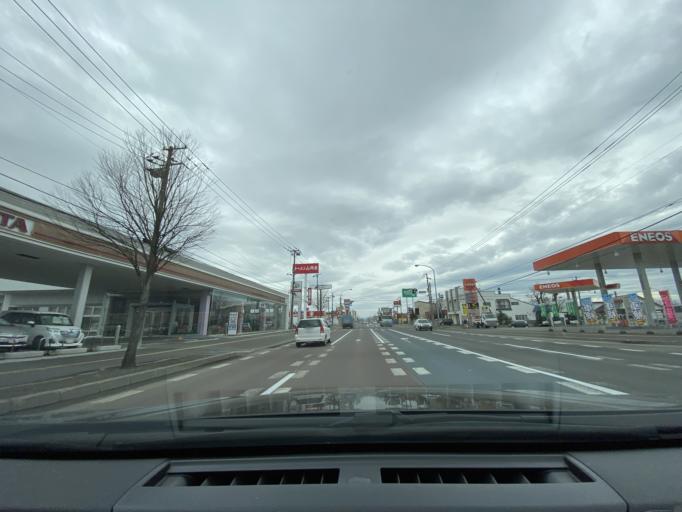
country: JP
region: Hokkaido
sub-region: Asahikawa-shi
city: Asahikawa
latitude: 43.8049
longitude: 142.4249
